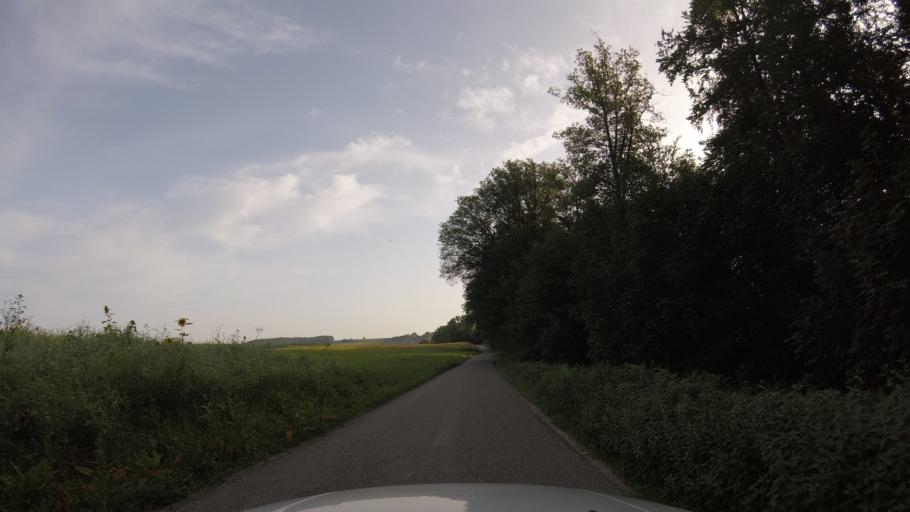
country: DE
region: Baden-Wuerttemberg
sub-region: Regierungsbezirk Stuttgart
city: Spiegelberg
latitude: 49.0215
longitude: 9.4000
